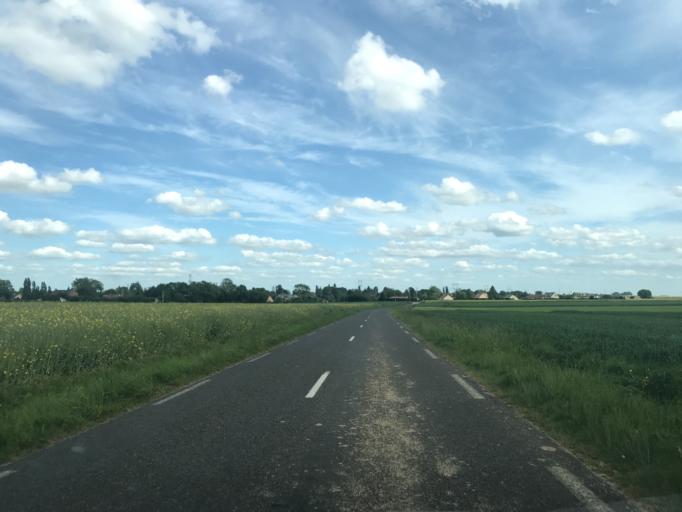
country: FR
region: Haute-Normandie
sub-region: Departement de l'Eure
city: Beaumont-le-Roger
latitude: 49.1493
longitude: 0.8241
